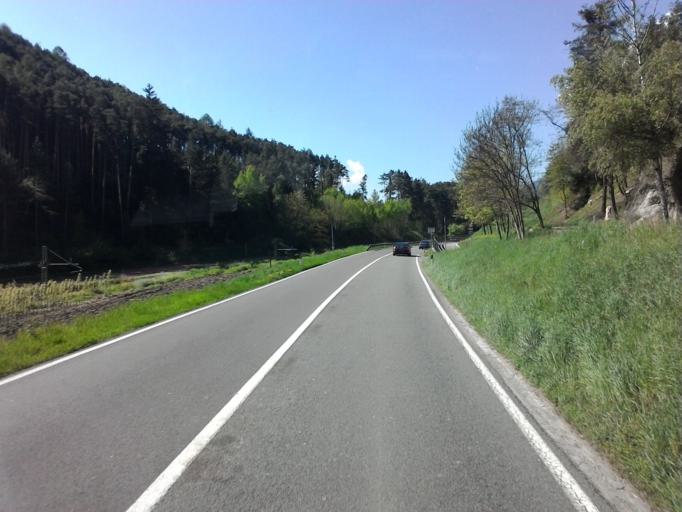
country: IT
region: Trentino-Alto Adige
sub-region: Bolzano
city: Naz-Sciaves - Natz-Schabs
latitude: 46.7787
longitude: 11.6688
